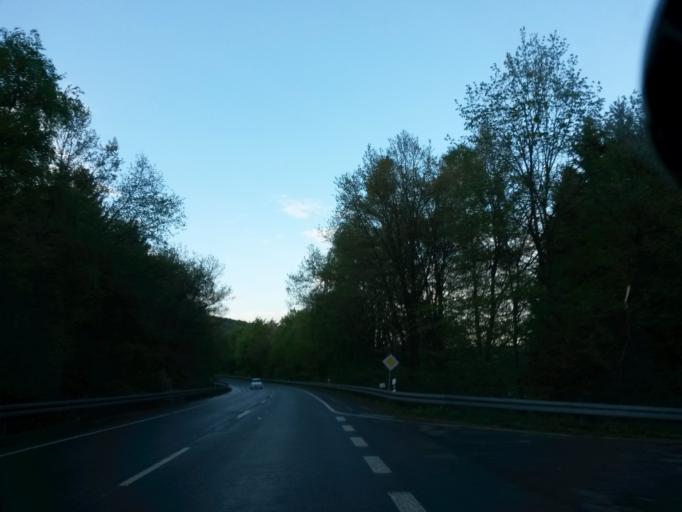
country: DE
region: North Rhine-Westphalia
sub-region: Regierungsbezirk Arnsberg
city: Herscheid
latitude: 51.1539
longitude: 7.7429
